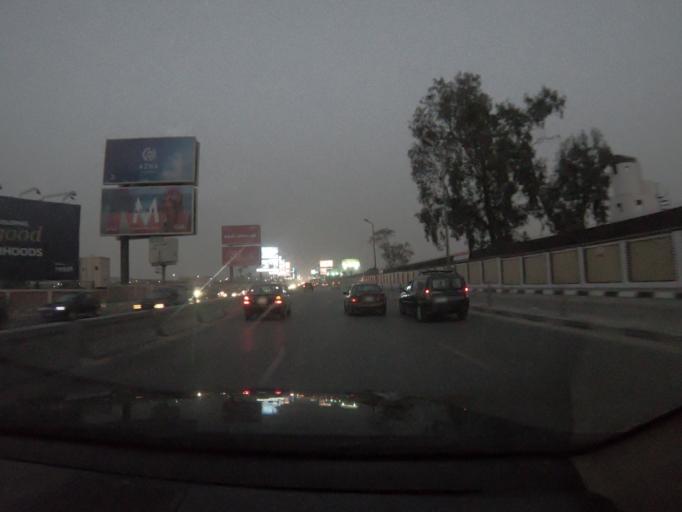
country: EG
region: Muhafazat al Qalyubiyah
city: Al Khankah
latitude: 30.0807
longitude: 31.3941
